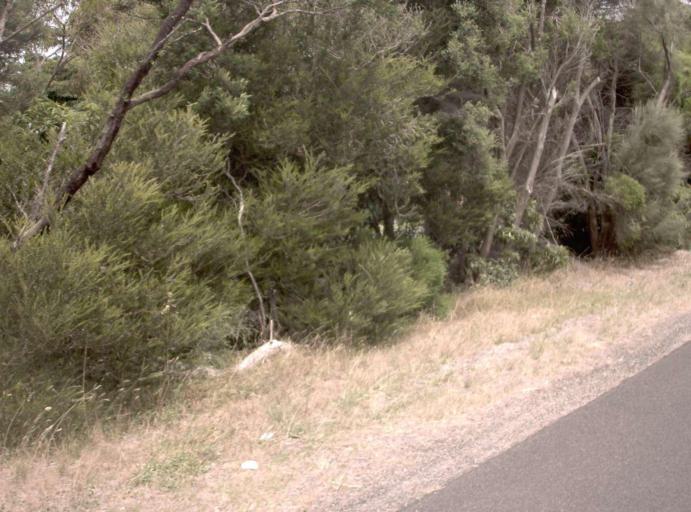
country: AU
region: Victoria
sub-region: Mornington Peninsula
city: Rosebud
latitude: -38.3650
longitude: 144.9167
